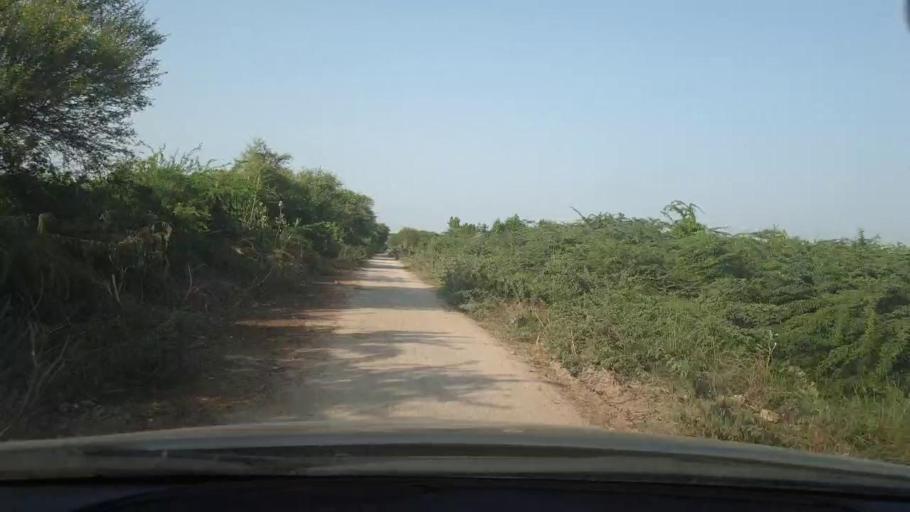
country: PK
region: Sindh
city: Naukot
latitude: 24.7815
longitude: 69.2344
